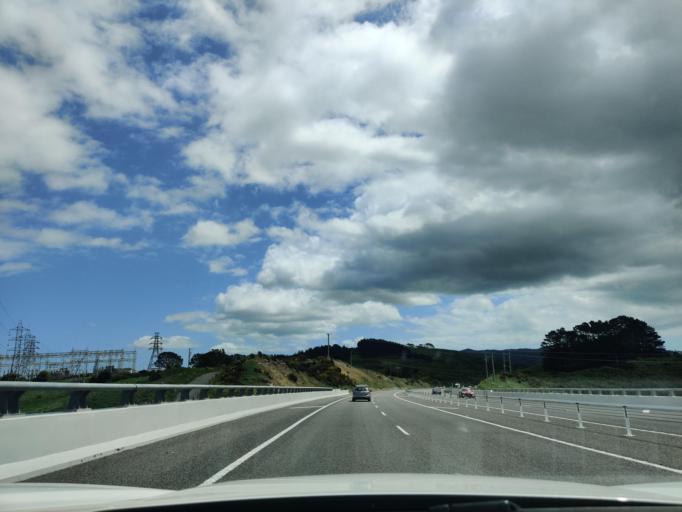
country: NZ
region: Wellington
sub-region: Porirua City
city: Porirua
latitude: -41.1556
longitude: 174.8746
